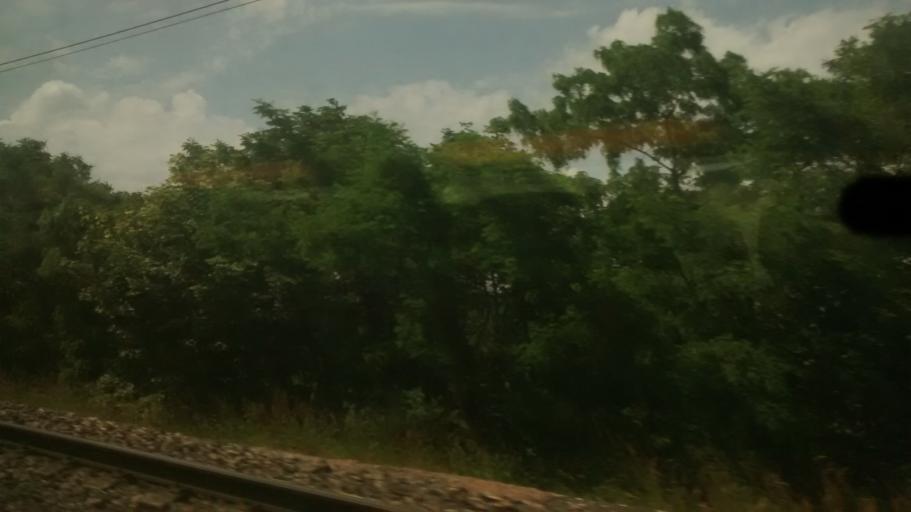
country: FR
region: Bourgogne
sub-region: Departement de Saone-et-Loire
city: Cluny
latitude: 46.4080
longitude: 4.6582
